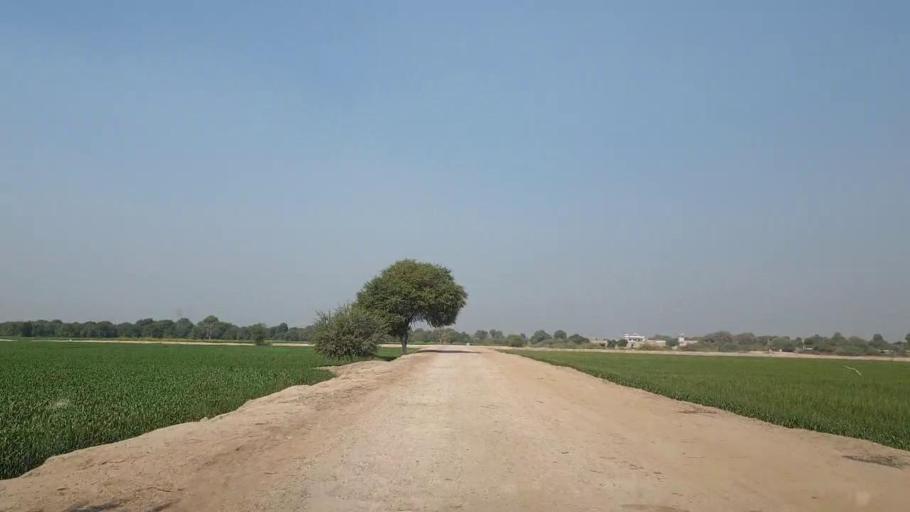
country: PK
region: Sindh
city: Tando Allahyar
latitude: 25.5018
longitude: 68.8342
